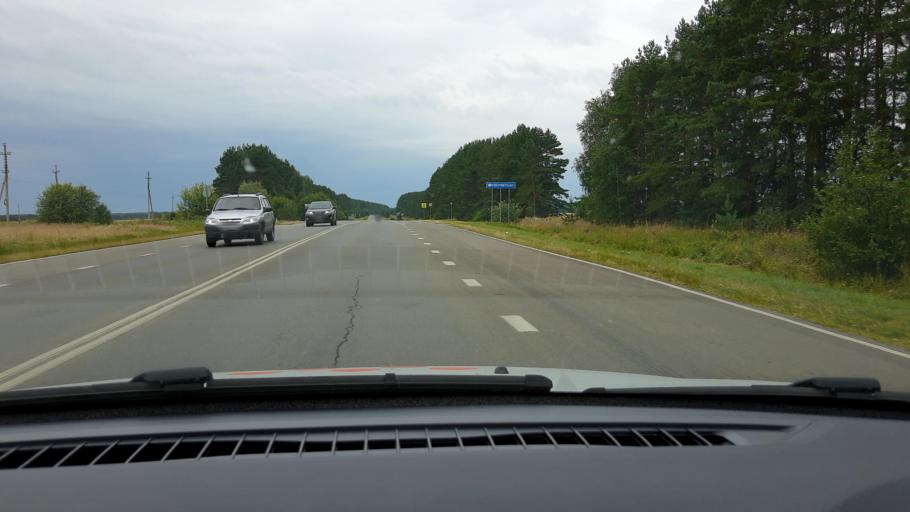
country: RU
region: Nizjnij Novgorod
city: Vyyezdnoye
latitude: 55.1735
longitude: 43.5973
